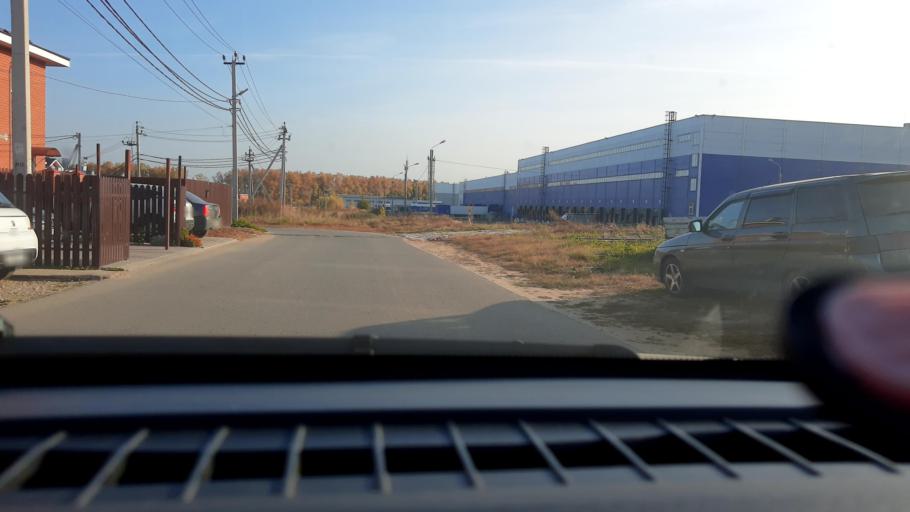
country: RU
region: Nizjnij Novgorod
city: Afonino
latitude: 56.2163
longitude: 44.0831
